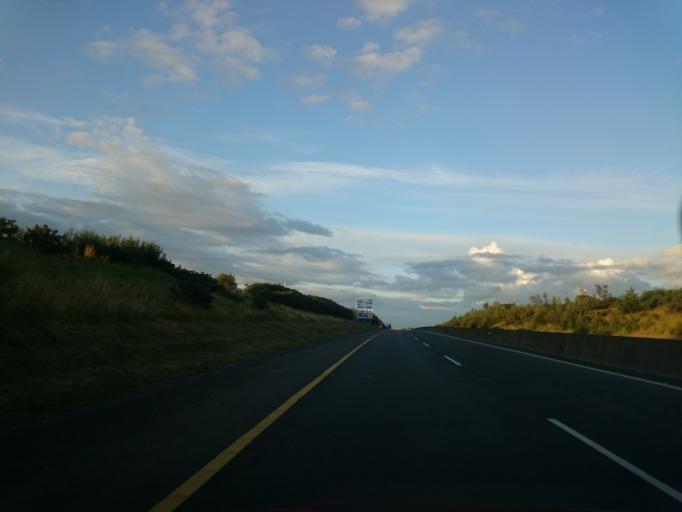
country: IE
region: Leinster
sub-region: Loch Garman
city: Castletown
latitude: 52.7415
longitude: -6.2235
